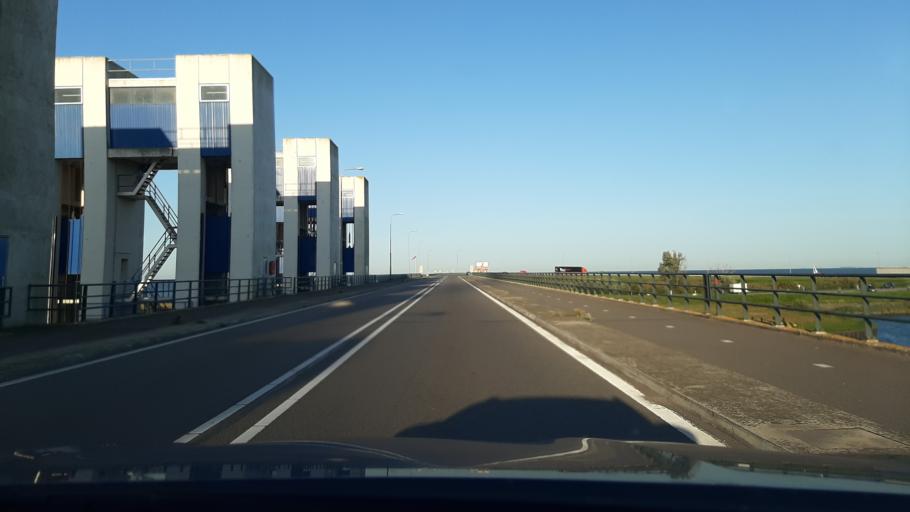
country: NL
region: Flevoland
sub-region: Gemeente Lelystad
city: Lelystad
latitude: 52.5277
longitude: 5.4298
